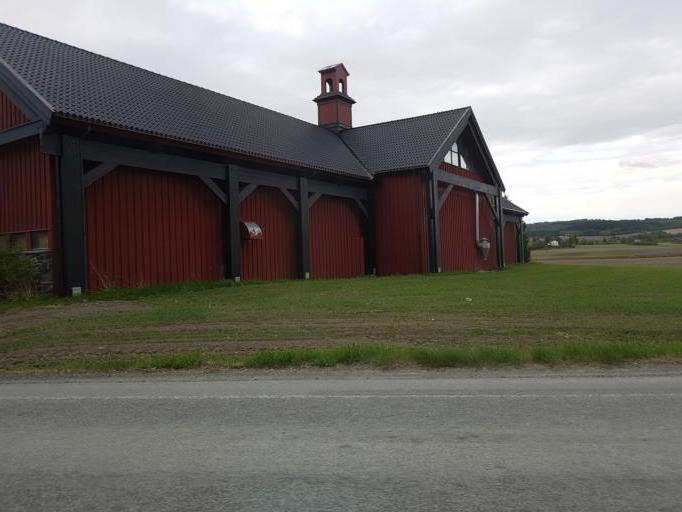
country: NO
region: Nord-Trondelag
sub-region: Levanger
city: Levanger
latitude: 63.7401
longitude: 11.2838
